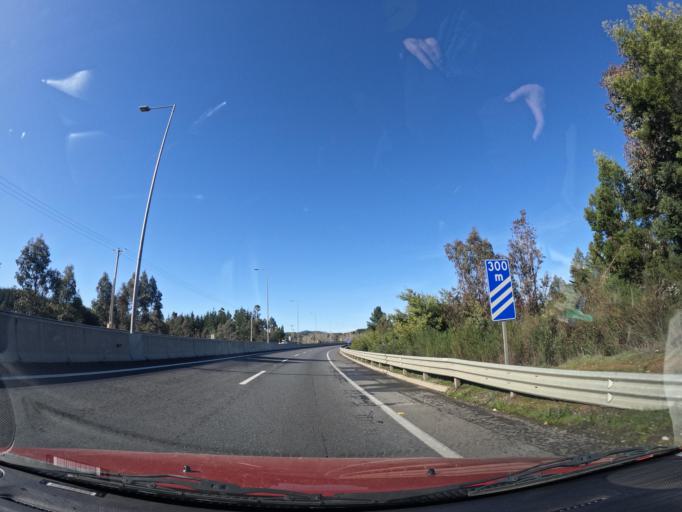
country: CL
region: Biobio
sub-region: Provincia de Concepcion
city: Chiguayante
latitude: -36.9031
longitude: -72.7815
